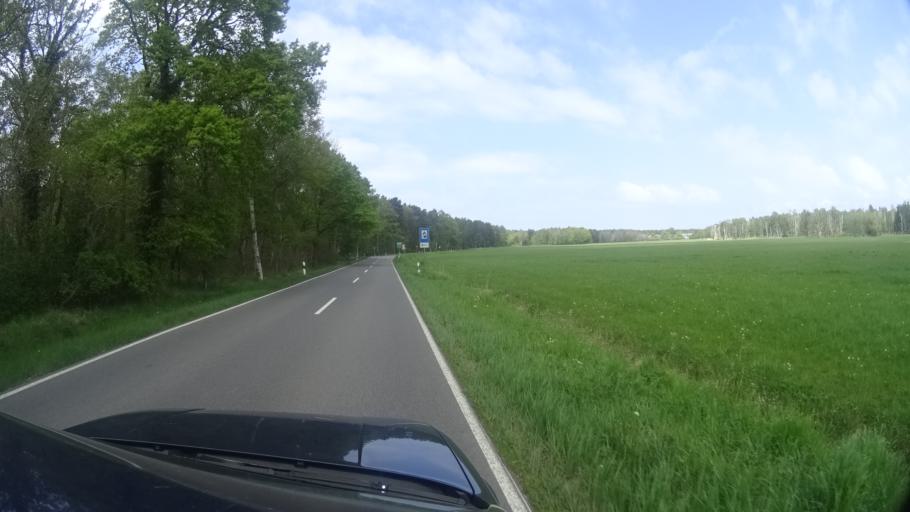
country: DE
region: Mecklenburg-Vorpommern
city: Ostseebad Dierhagen
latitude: 54.2799
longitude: 12.3221
